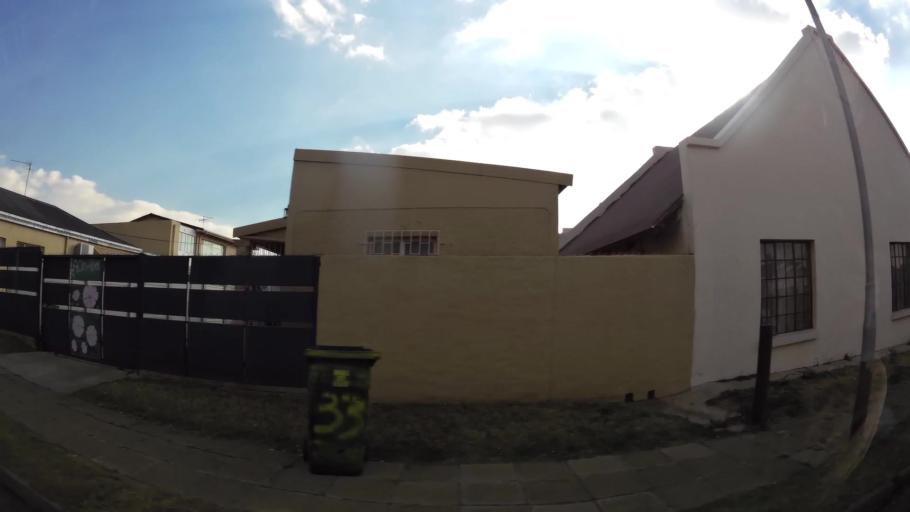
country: ZA
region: Gauteng
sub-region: West Rand District Municipality
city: Krugersdorp
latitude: -26.0999
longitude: 27.7529
